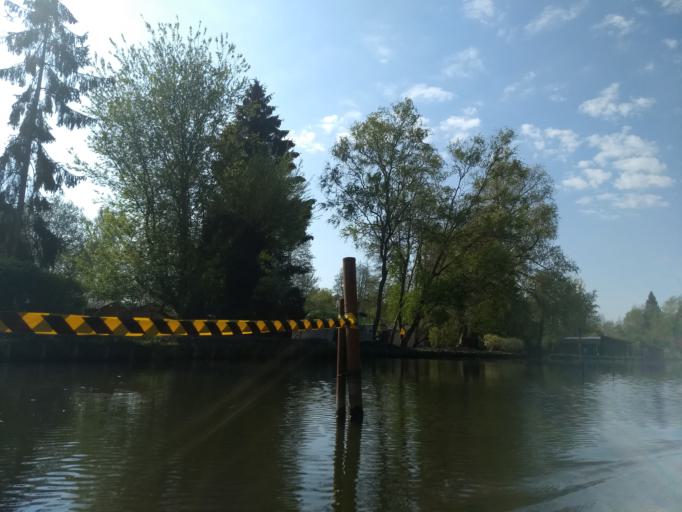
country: FR
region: Picardie
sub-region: Departement de la Somme
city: Rivery
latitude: 49.8962
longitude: 2.3277
